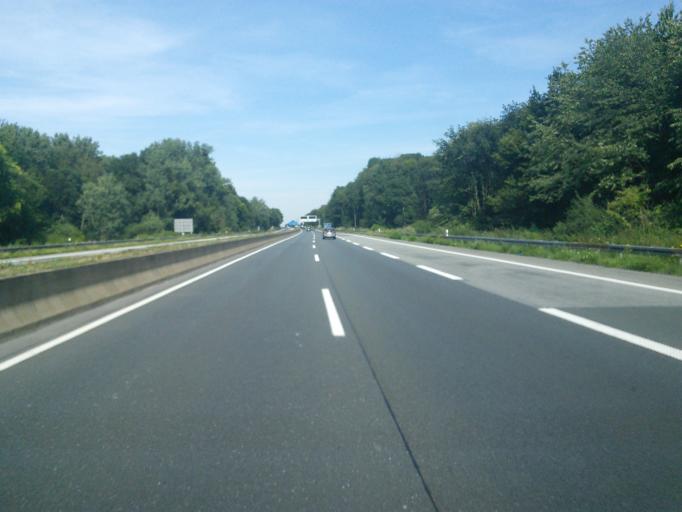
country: DE
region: North Rhine-Westphalia
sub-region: Regierungsbezirk Dusseldorf
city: Monchengladbach
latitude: 51.2335
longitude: 6.4542
